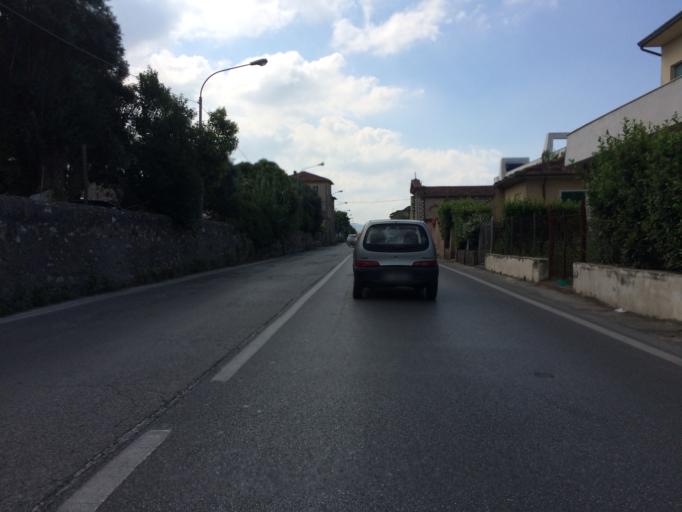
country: IT
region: Tuscany
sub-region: Provincia di Lucca
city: Ripa-Pozzi-Querceta-Ponterosso
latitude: 43.9728
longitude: 10.2054
